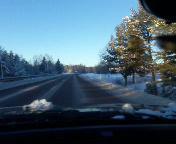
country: SE
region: Gaevleborg
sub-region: Ljusdals Kommun
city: Ljusdal
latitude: 61.7848
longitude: 16.1346
